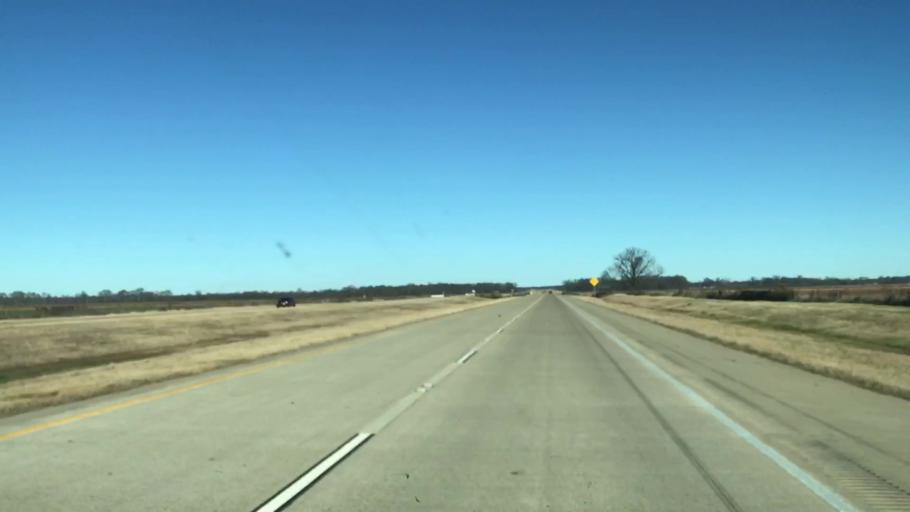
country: US
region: Louisiana
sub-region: Caddo Parish
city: Oil City
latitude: 32.7283
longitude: -93.8723
